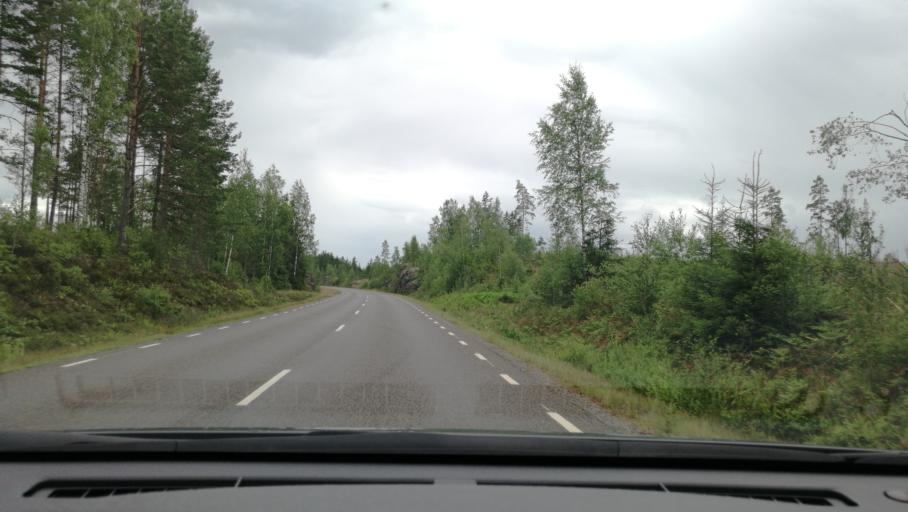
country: SE
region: OEstergoetland
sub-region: Norrkopings Kommun
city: Svartinge
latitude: 58.8049
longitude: 15.9414
